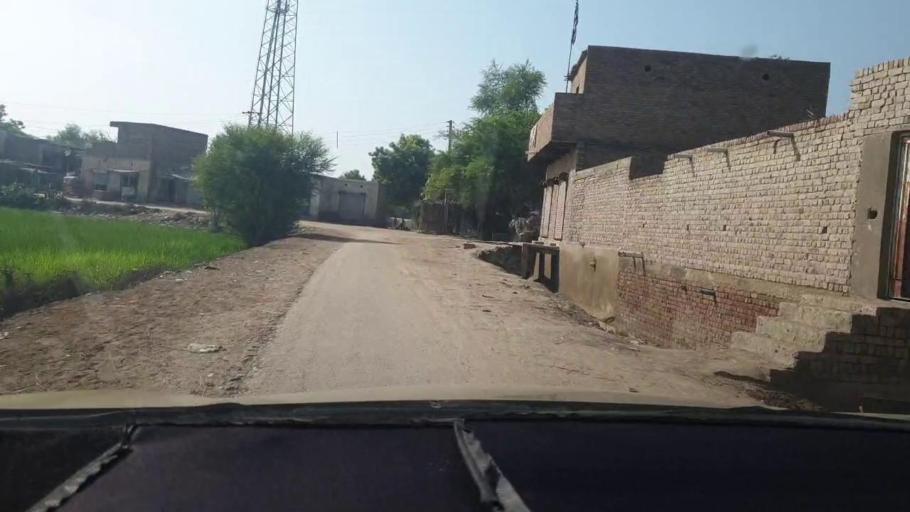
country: PK
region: Sindh
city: Kambar
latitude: 27.6083
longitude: 68.0925
